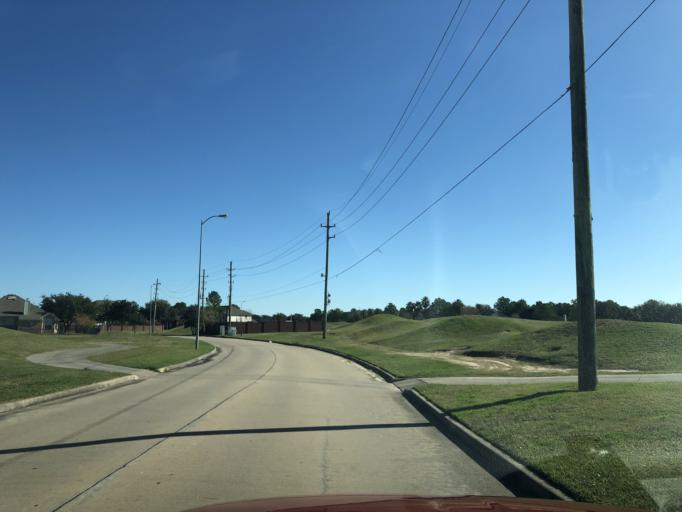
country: US
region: Texas
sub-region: Harris County
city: Oak Cliff Place
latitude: 29.9369
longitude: -95.6666
